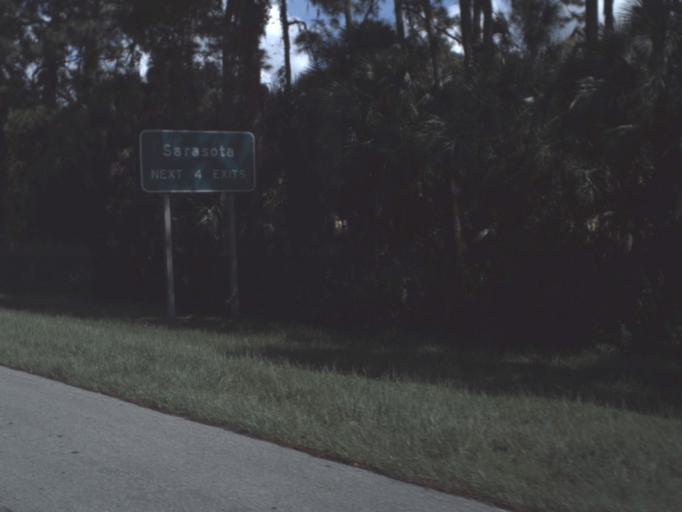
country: US
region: Florida
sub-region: Sarasota County
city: Osprey
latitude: 27.2135
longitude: -82.4449
